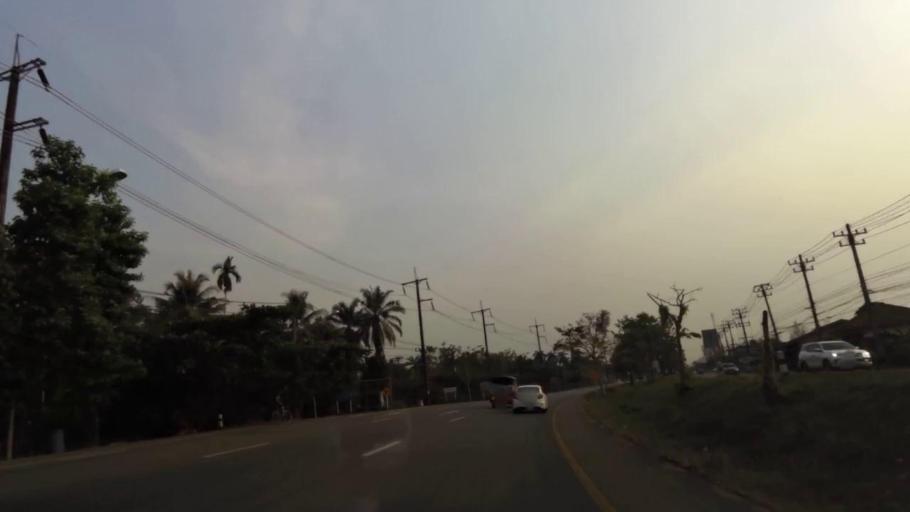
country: TH
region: Chanthaburi
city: Khlung
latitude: 12.5128
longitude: 102.1689
